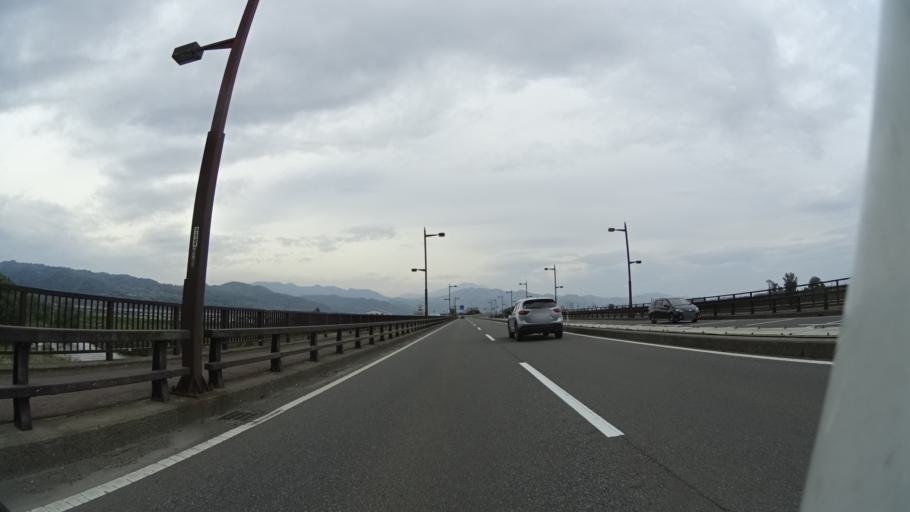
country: JP
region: Nagano
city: Nagano-shi
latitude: 36.5581
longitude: 138.1383
